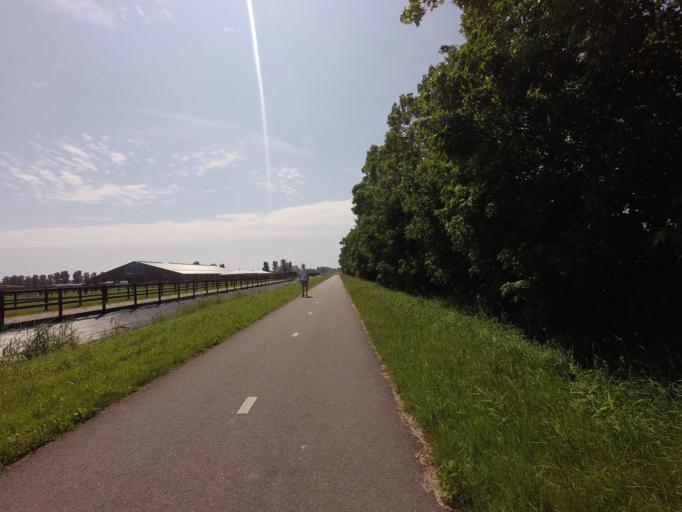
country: NL
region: North Holland
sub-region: Gemeente Enkhuizen
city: Enkhuizen
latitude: 52.7140
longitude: 5.2290
